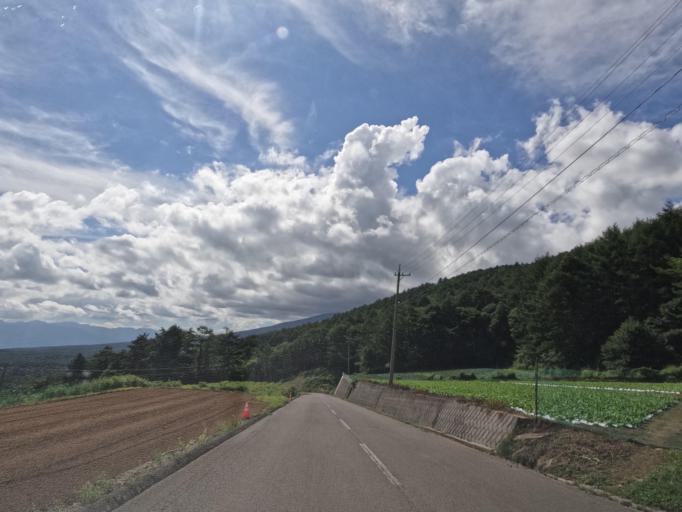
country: JP
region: Yamanashi
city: Nirasaki
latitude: 35.9220
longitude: 138.4581
